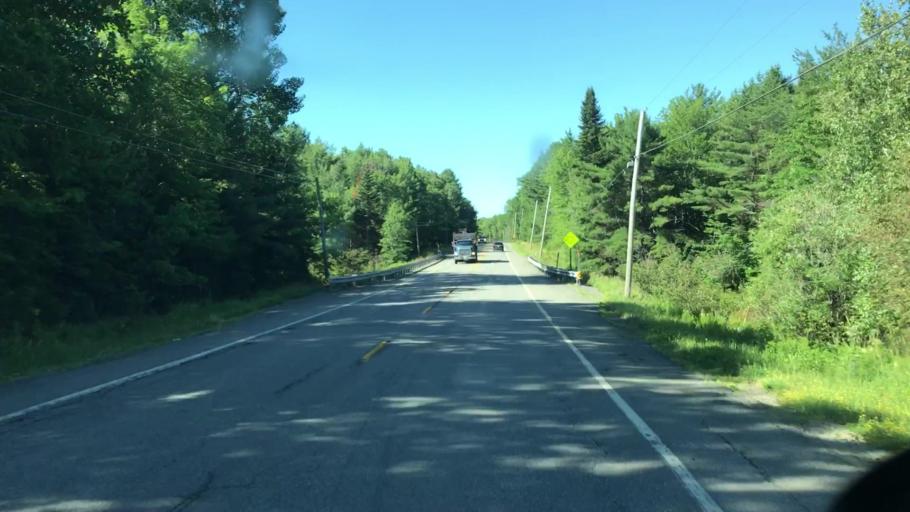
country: US
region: Maine
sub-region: Penobscot County
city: Howland
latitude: 45.2763
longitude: -68.6342
